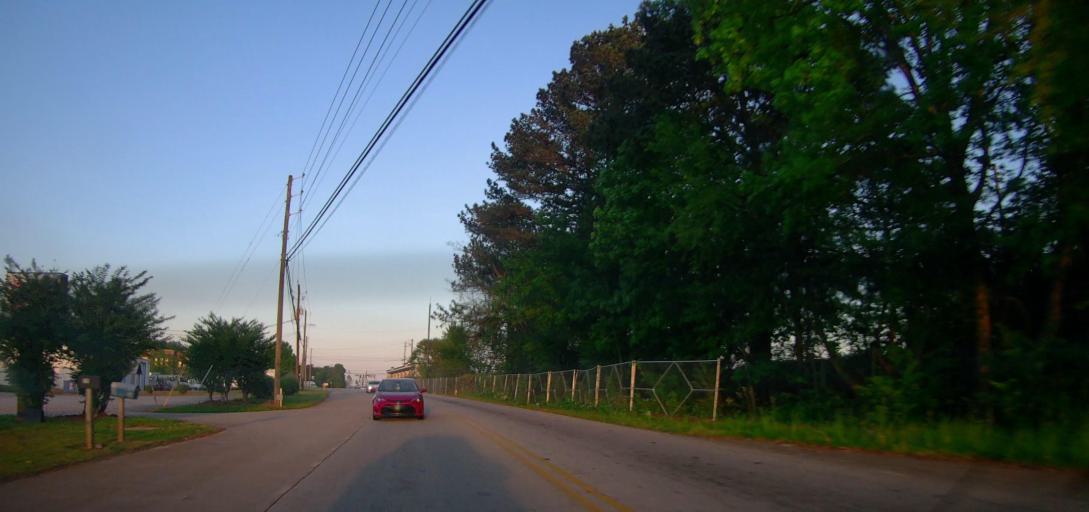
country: US
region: Georgia
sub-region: Henry County
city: McDonough
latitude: 33.4143
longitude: -84.1596
